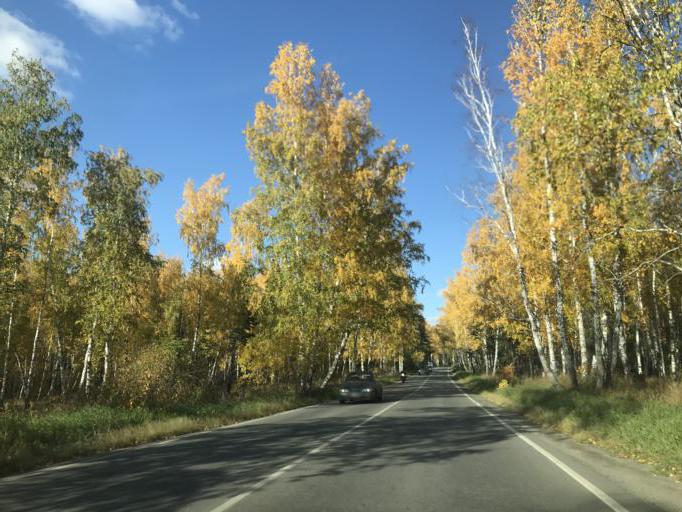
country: RU
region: Chelyabinsk
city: Dolgoderevenskoye
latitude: 55.2753
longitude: 61.3649
